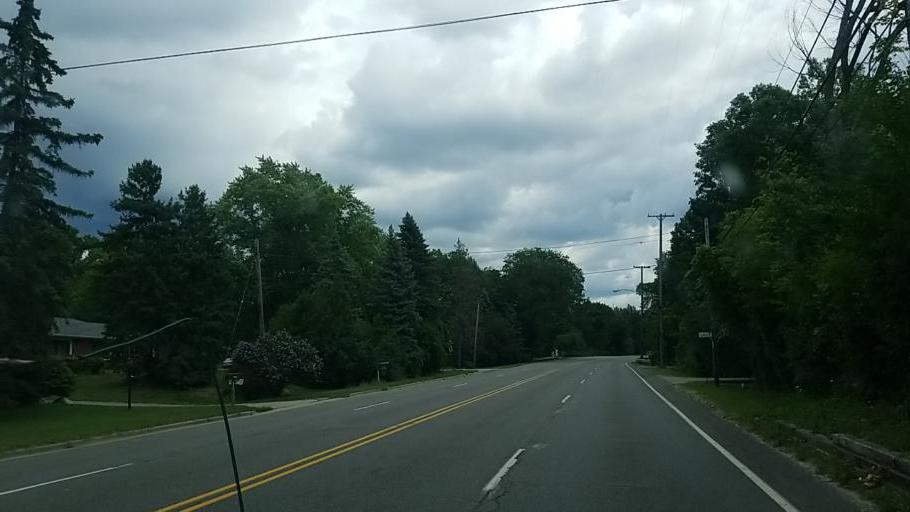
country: US
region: Michigan
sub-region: Kent County
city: East Grand Rapids
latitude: 42.9551
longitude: -85.5851
